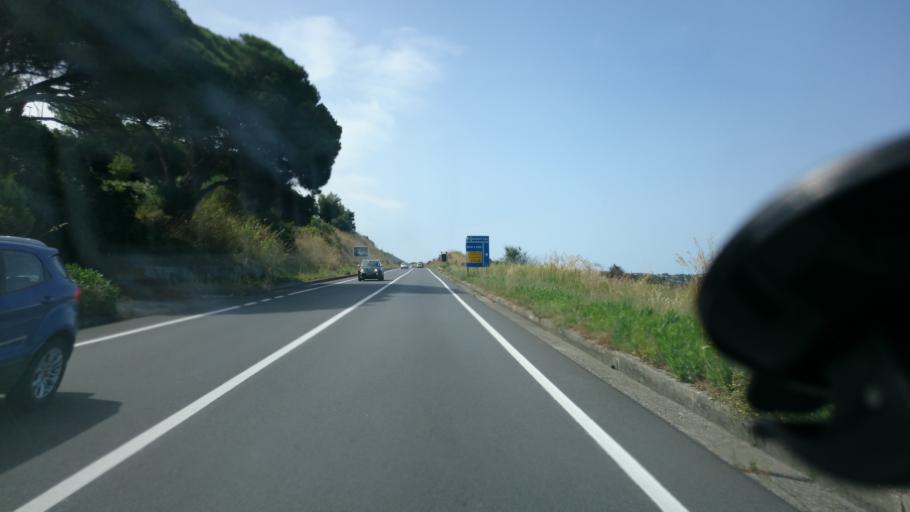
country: IT
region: Calabria
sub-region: Provincia di Cosenza
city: San Nicola Arcella
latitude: 39.8657
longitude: 15.7965
